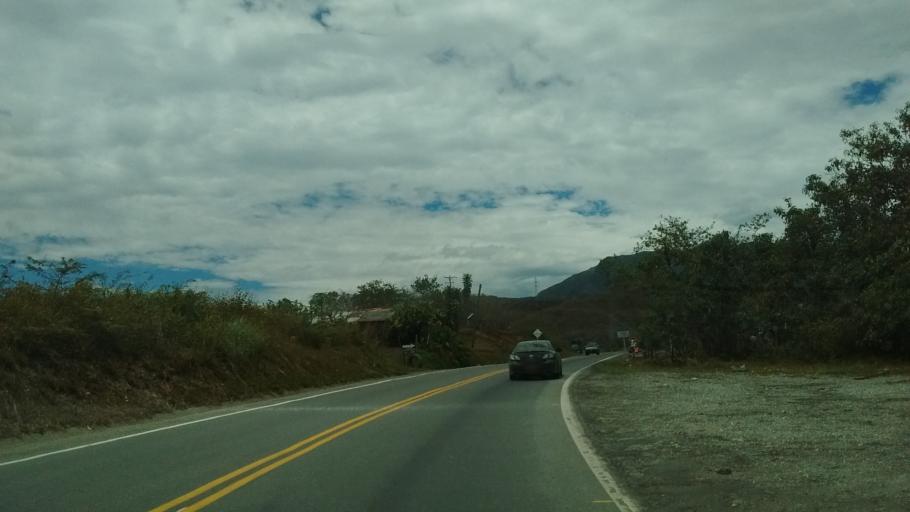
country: CO
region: Cauca
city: La Sierra
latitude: 2.2195
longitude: -76.7994
